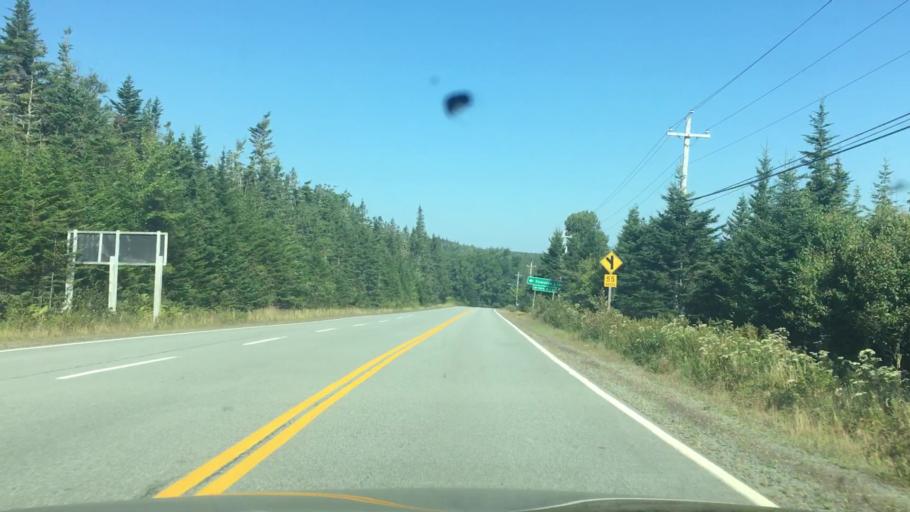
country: CA
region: Nova Scotia
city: New Glasgow
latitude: 44.8187
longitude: -62.6337
